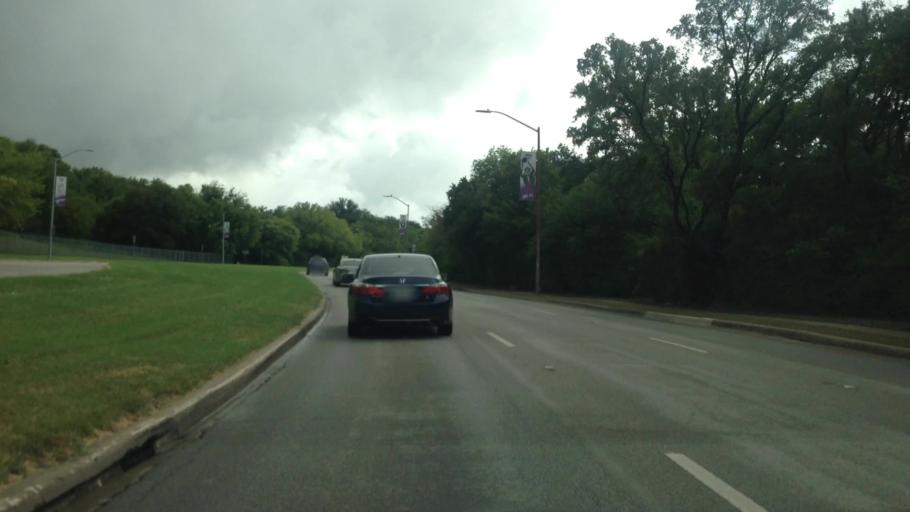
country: US
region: Texas
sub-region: Tarrant County
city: Westworth
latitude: 32.7018
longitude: -97.3902
